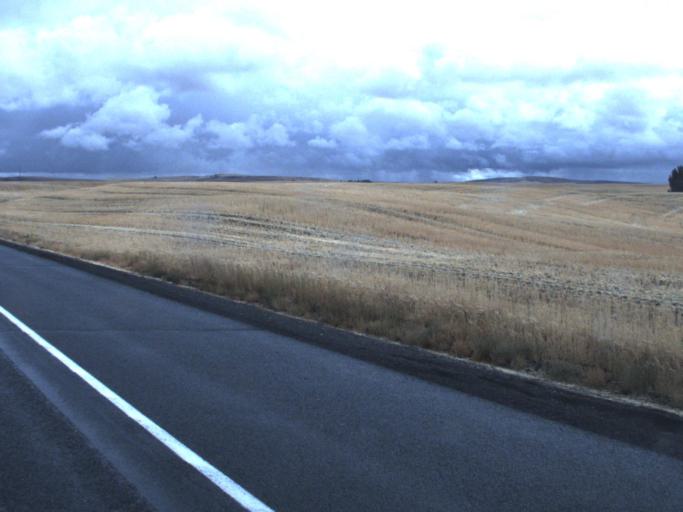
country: US
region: Washington
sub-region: Lincoln County
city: Davenport
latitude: 47.6577
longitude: -117.9786
